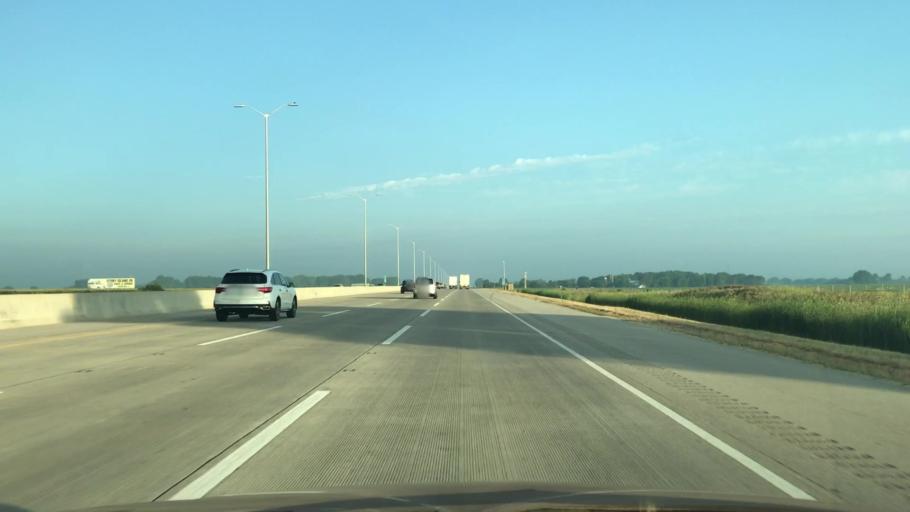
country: US
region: Illinois
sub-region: DeKalb County
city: Kingston
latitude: 42.2127
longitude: -88.7255
